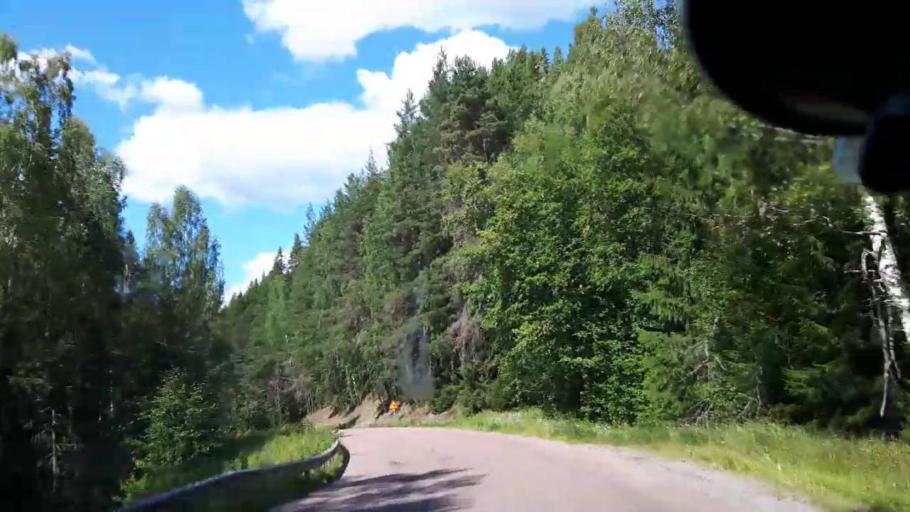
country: SE
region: Jaemtland
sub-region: Ragunda Kommun
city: Hammarstrand
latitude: 63.0131
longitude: 16.6341
